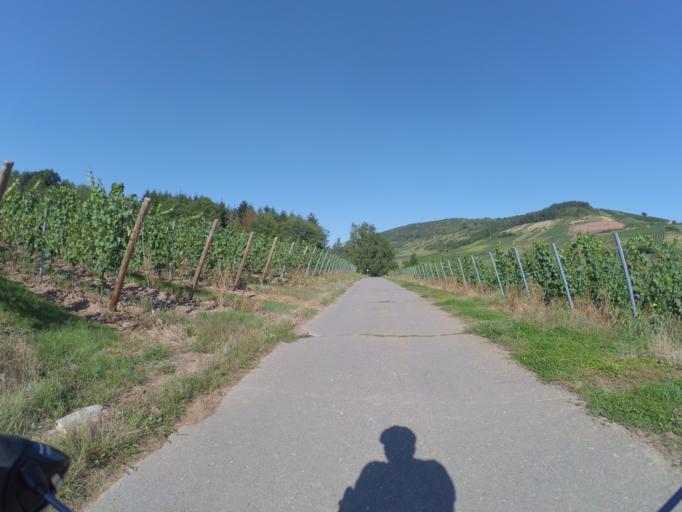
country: DE
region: Rheinland-Pfalz
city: Rivenich
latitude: 49.8657
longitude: 6.8467
